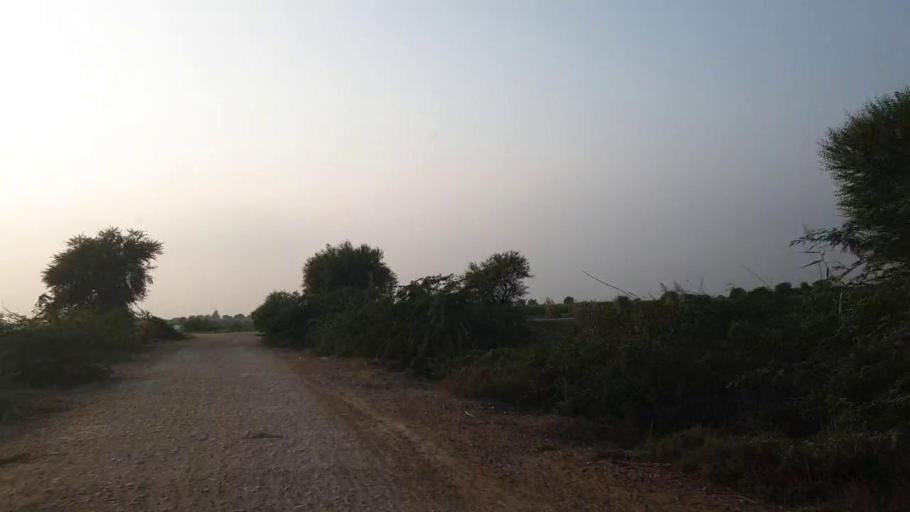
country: PK
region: Sindh
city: Tando Ghulam Ali
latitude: 25.0670
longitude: 68.9603
